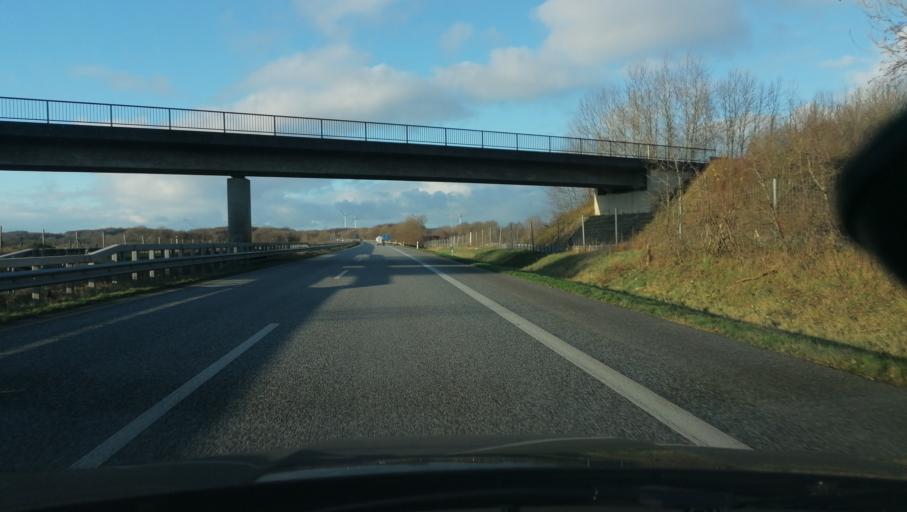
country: DE
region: Schleswig-Holstein
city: Hadenfeld
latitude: 54.0217
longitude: 9.4590
